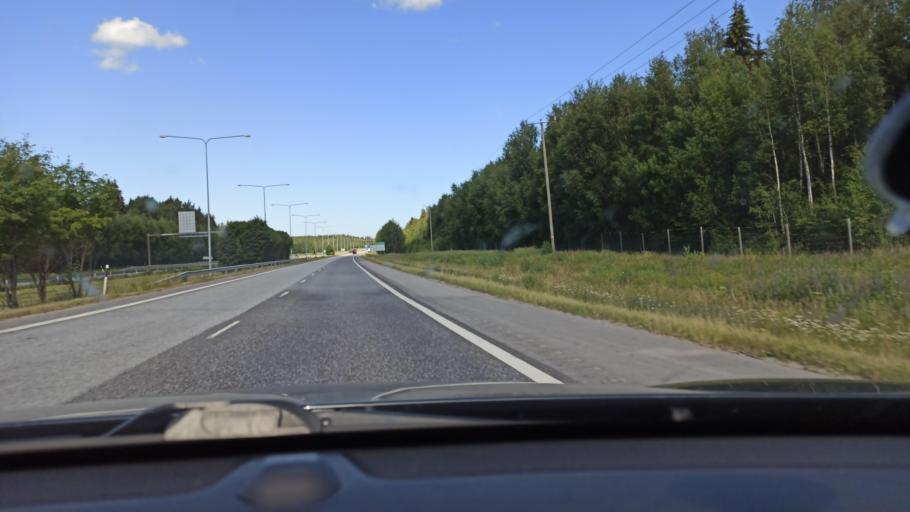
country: FI
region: Ostrobothnia
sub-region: Vaasa
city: Ristinummi
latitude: 63.0412
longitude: 21.7308
